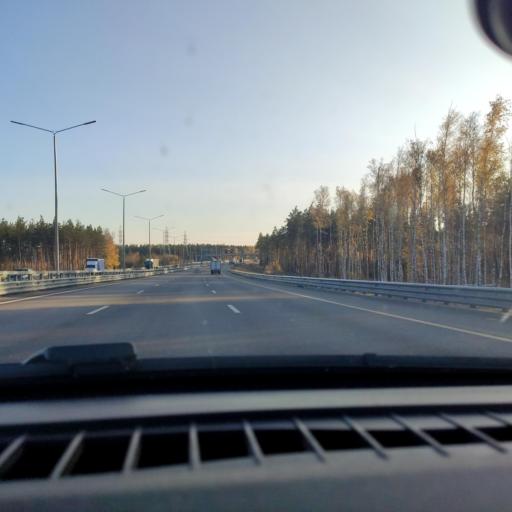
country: RU
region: Voronezj
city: Somovo
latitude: 51.7319
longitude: 39.3105
